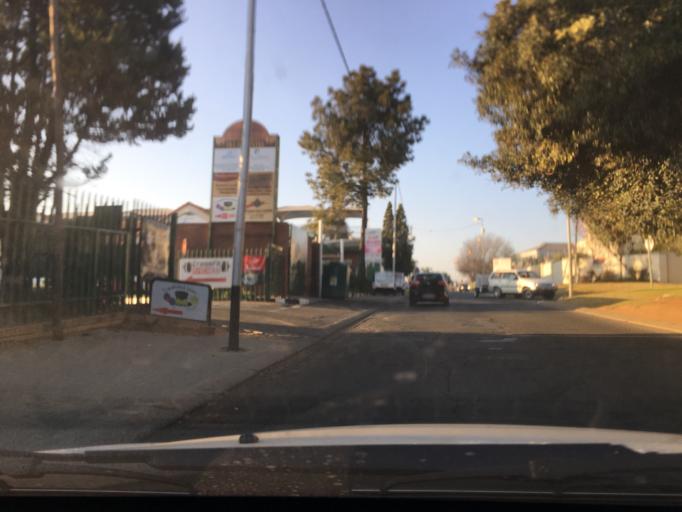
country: ZA
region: Gauteng
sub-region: City of Johannesburg Metropolitan Municipality
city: Johannesburg
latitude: -26.0737
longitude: 28.0112
